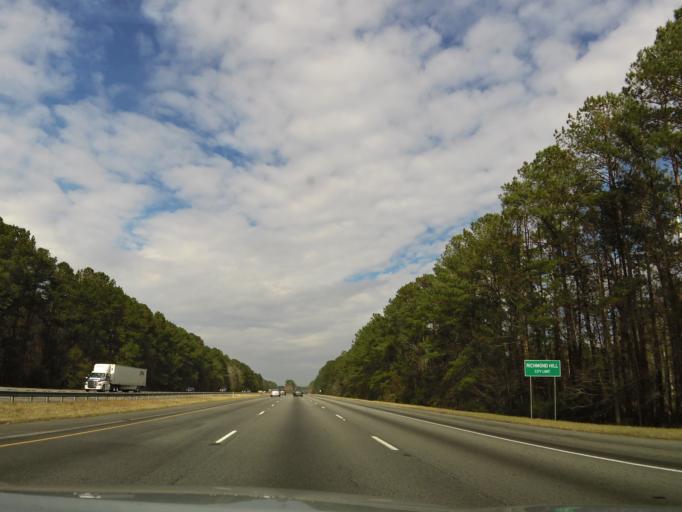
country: US
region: Georgia
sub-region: Bryan County
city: Richmond Hill
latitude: 31.8545
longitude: -81.3414
